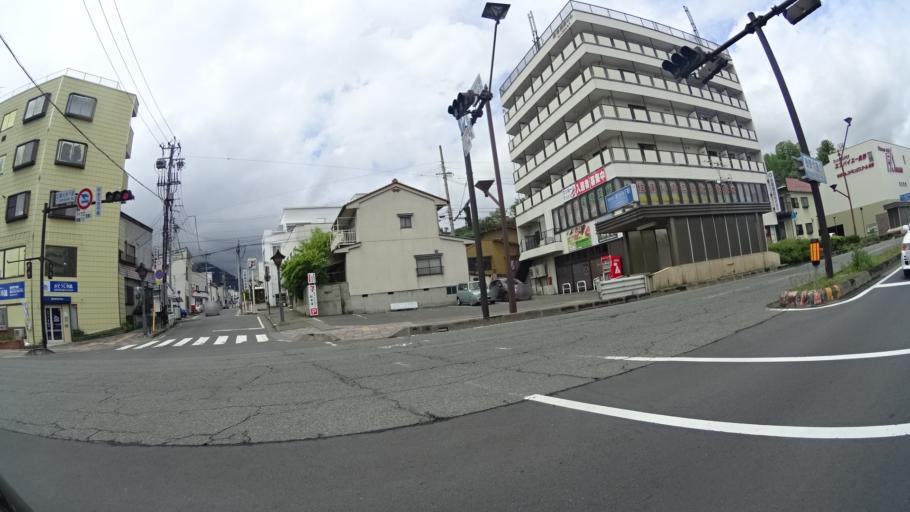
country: JP
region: Nagano
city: Nagano-shi
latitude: 36.6587
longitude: 138.1937
